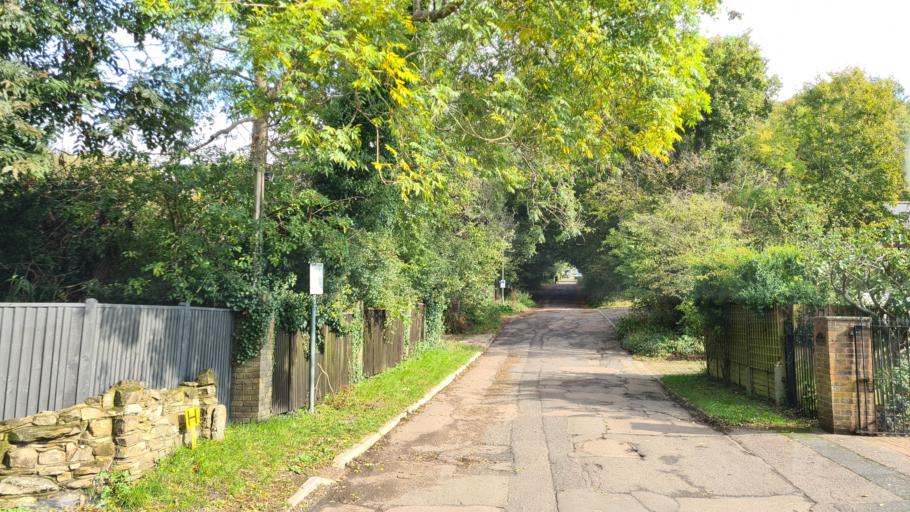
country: GB
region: England
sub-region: East Sussex
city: Hastings
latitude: 50.8805
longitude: 0.5641
